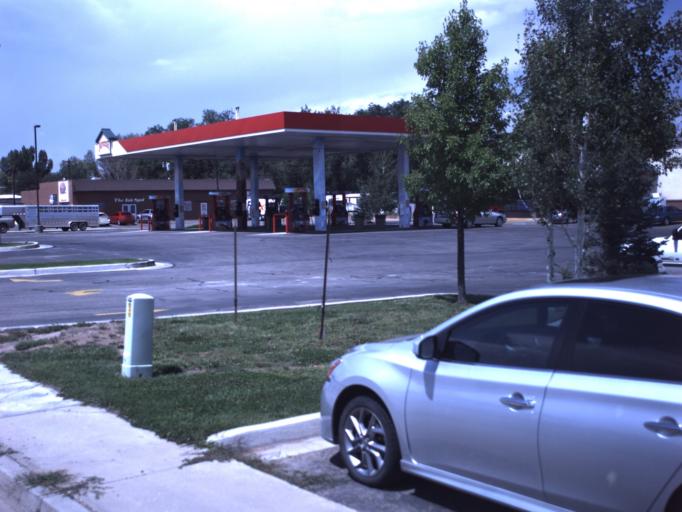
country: US
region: Utah
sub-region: Duchesne County
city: Roosevelt
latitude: 40.3023
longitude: -109.9756
